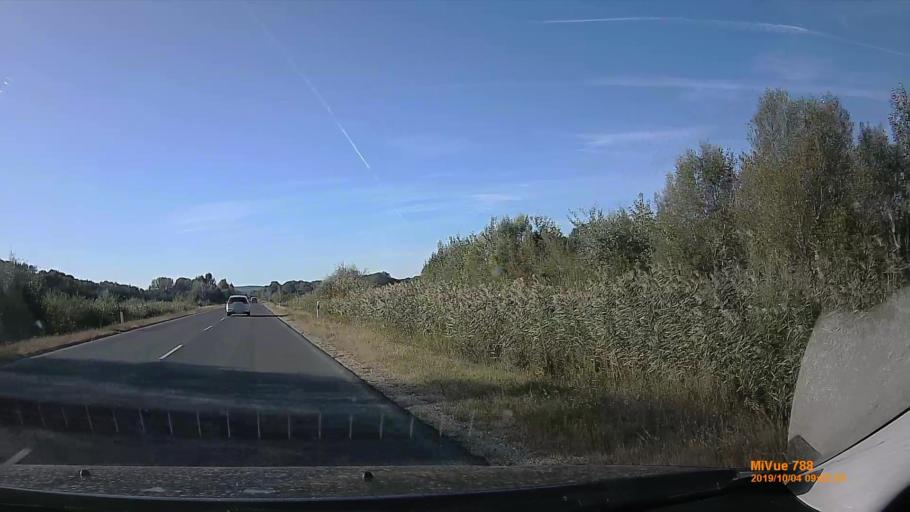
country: HU
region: Somogy
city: Karad
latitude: 46.7185
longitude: 17.7745
